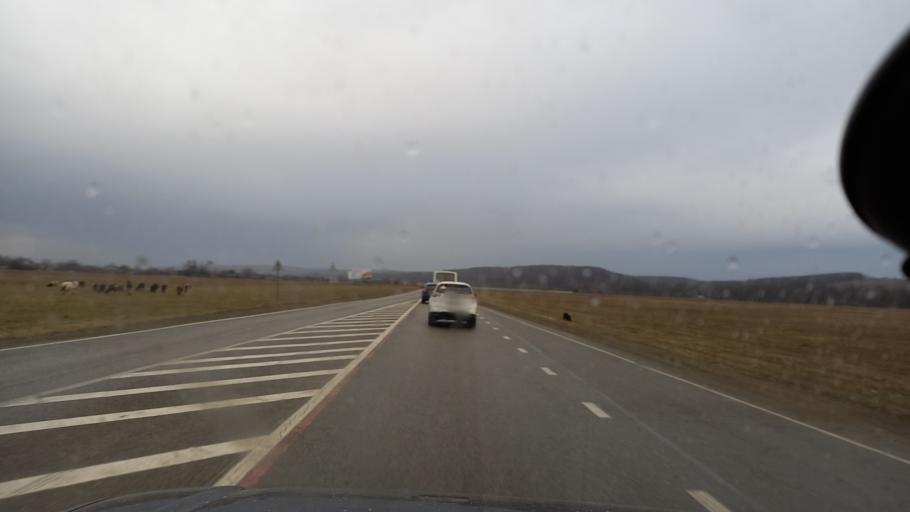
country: RU
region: Adygeya
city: Tul'skiy
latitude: 44.5377
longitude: 40.1405
